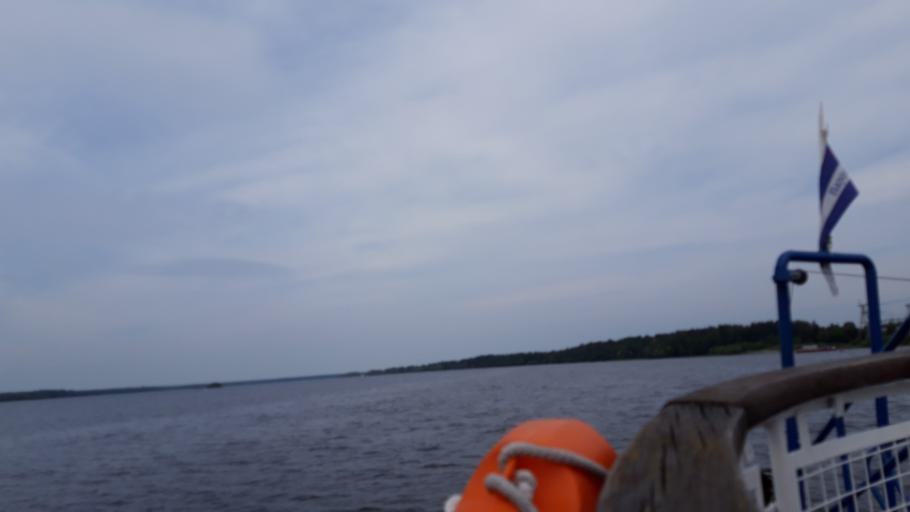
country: RU
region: Tverskaya
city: Konakovo
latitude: 56.7363
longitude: 36.7666
